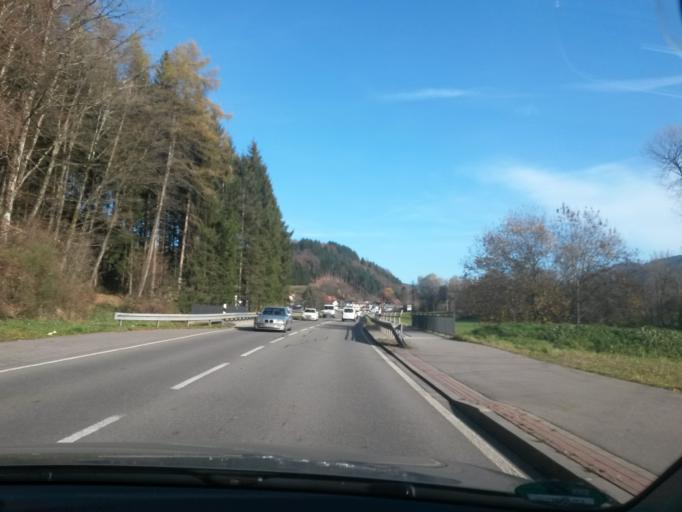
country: DE
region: Baden-Wuerttemberg
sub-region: Freiburg Region
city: Elzach
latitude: 48.1643
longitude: 8.0567
